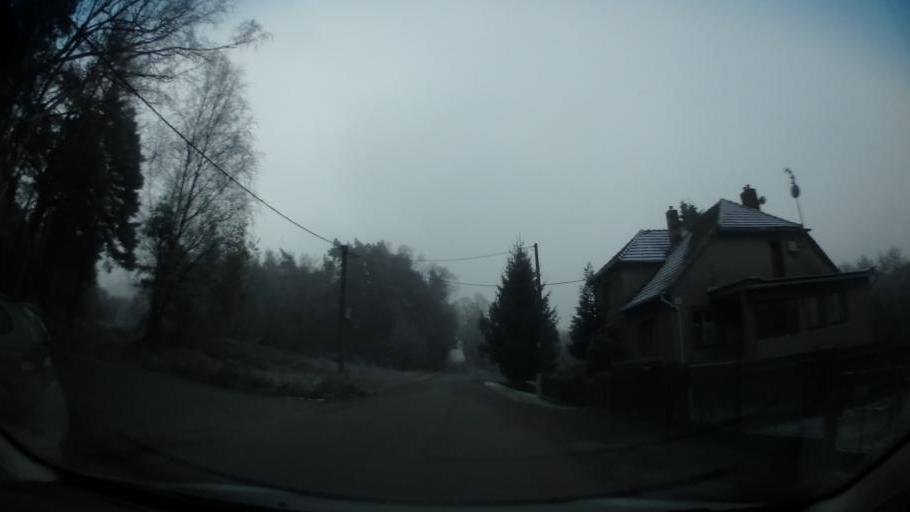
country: CZ
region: Vysocina
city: Budisov
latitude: 49.3033
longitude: 15.9506
